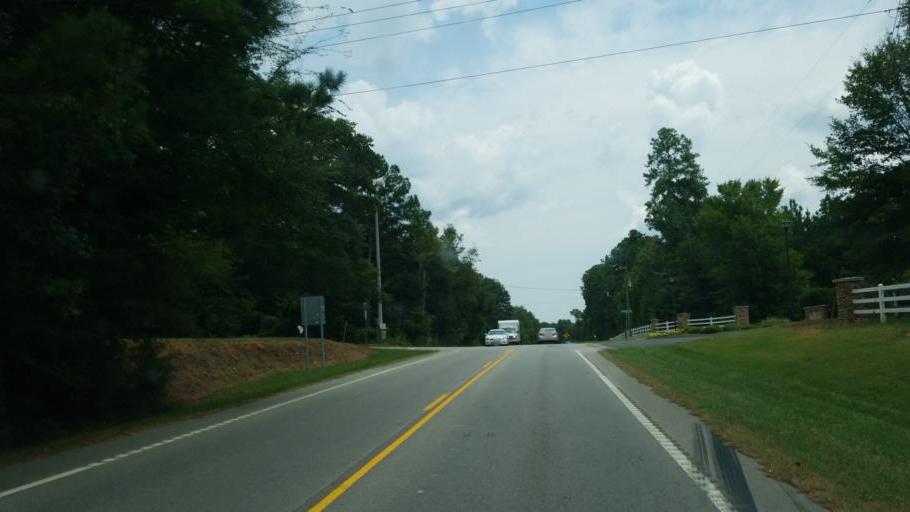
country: US
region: South Carolina
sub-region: York County
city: Newport
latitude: 34.9735
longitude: -81.1693
